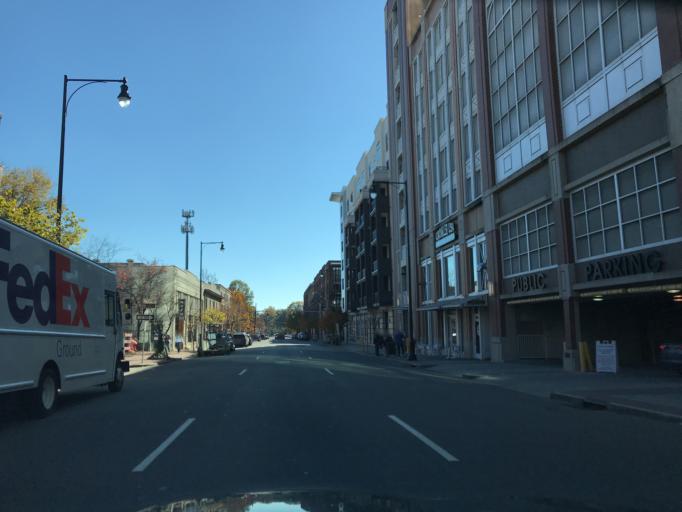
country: US
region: North Carolina
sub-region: Wake County
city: Raleigh
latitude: 35.7765
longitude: -78.6367
